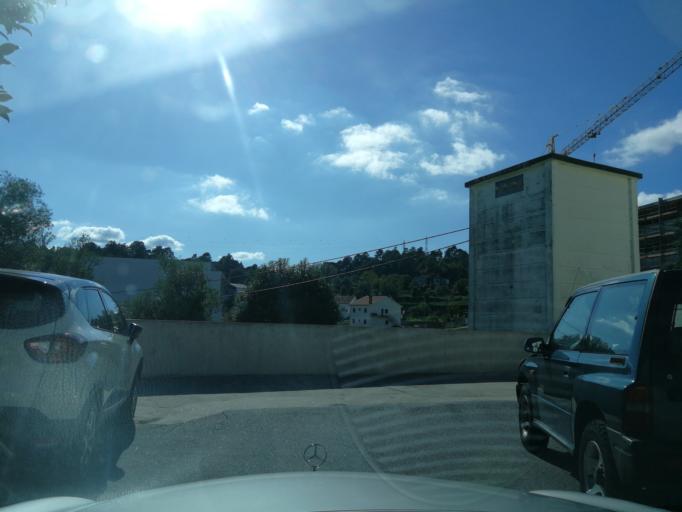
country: PT
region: Braga
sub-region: Braga
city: Adaufe
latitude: 41.5685
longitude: -8.3898
